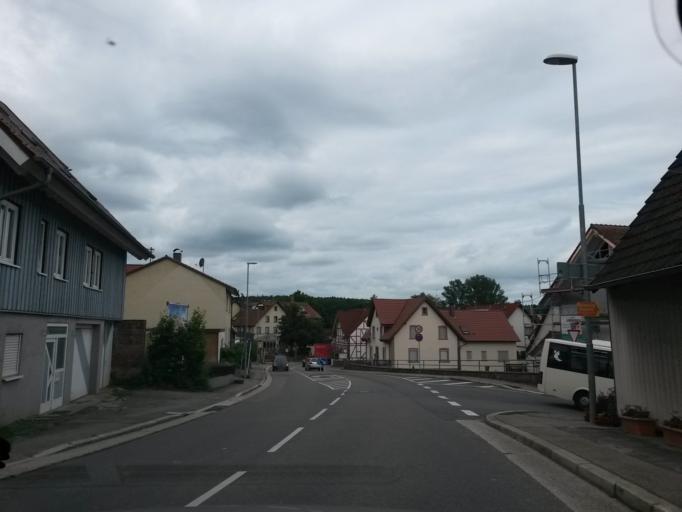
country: DE
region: Baden-Wuerttemberg
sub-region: Karlsruhe Region
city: Neuenburg
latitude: 48.9107
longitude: 8.5285
